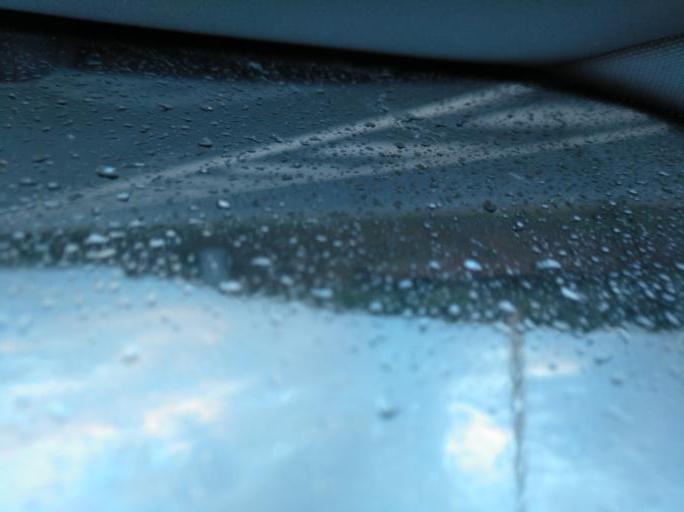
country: PT
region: Faro
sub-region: Castro Marim
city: Castro Marim
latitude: 37.2399
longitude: -7.4496
